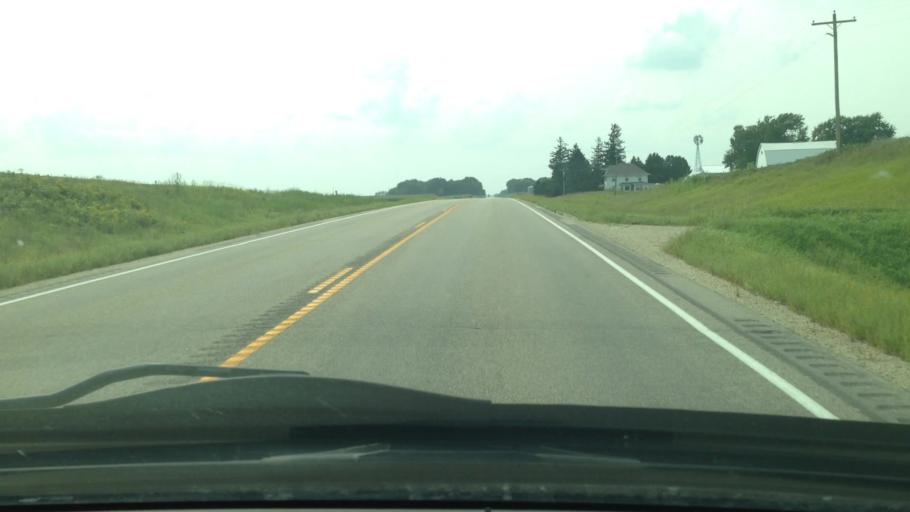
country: US
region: Minnesota
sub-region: Wabasha County
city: Plainview
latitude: 44.1652
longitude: -92.2020
